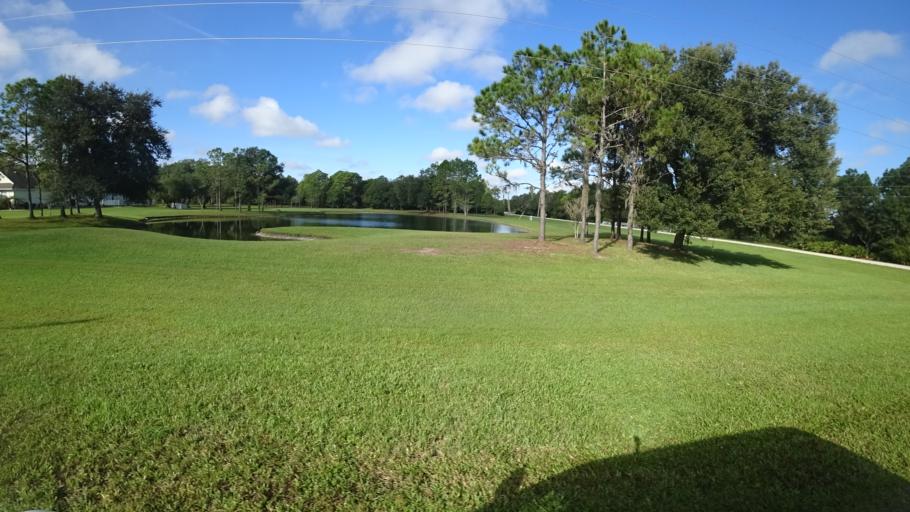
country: US
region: Florida
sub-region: Sarasota County
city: The Meadows
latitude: 27.4166
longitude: -82.3404
